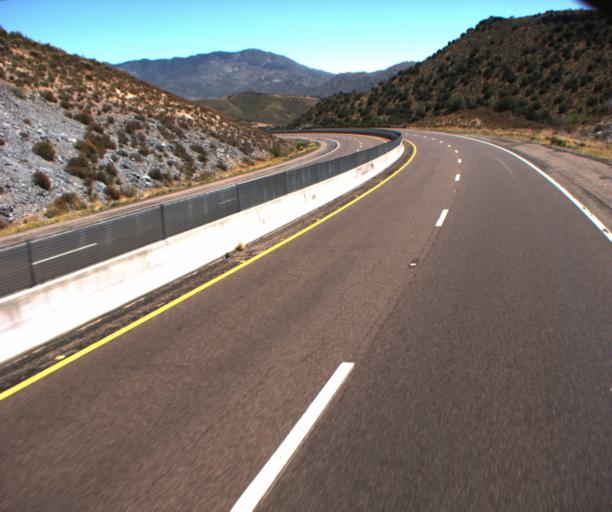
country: US
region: Arizona
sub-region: Gila County
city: Tonto Basin
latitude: 33.8977
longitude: -111.4581
